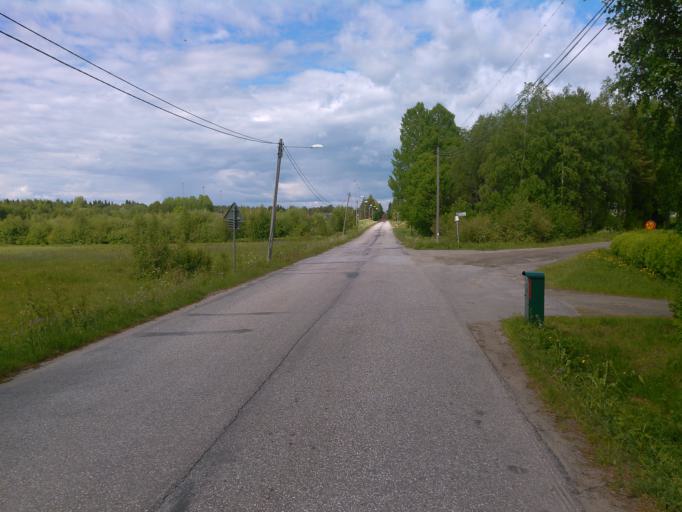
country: SE
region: Vaesterbotten
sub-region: Umea Kommun
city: Ersmark
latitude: 63.8785
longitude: 20.3199
